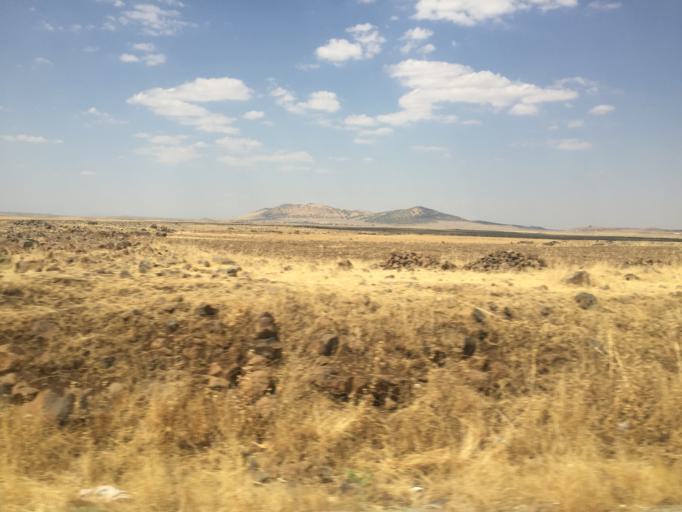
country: TR
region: Sanliurfa
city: Karacadag
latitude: 37.8449
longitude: 39.7052
